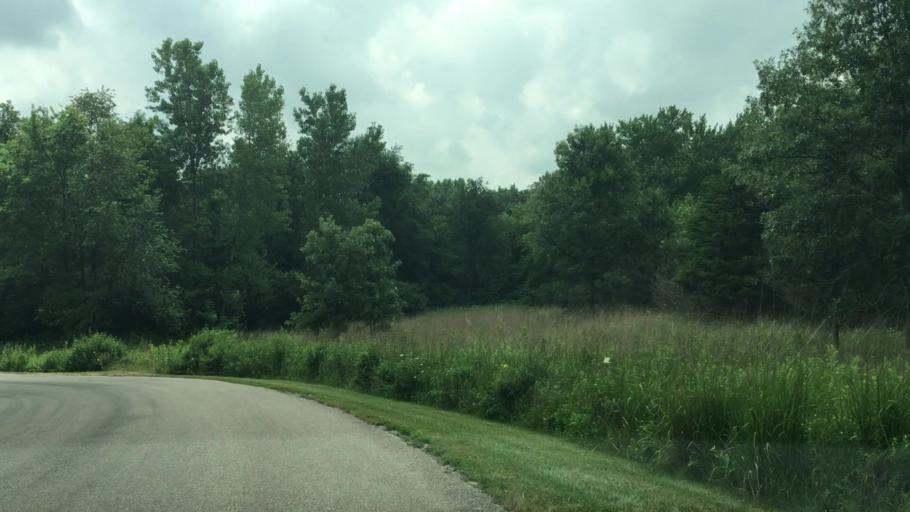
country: US
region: Iowa
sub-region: Johnson County
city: Tiffin
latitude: 41.7377
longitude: -91.7279
